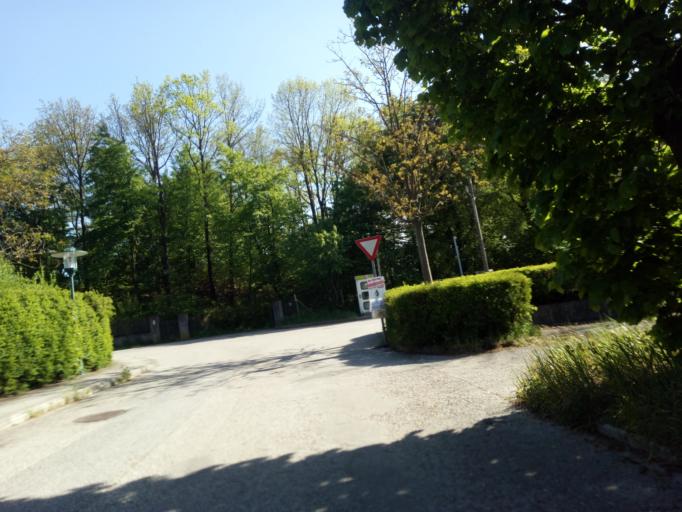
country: AT
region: Lower Austria
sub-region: Politischer Bezirk Modling
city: Laab im Walde
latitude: 48.1394
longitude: 16.1914
